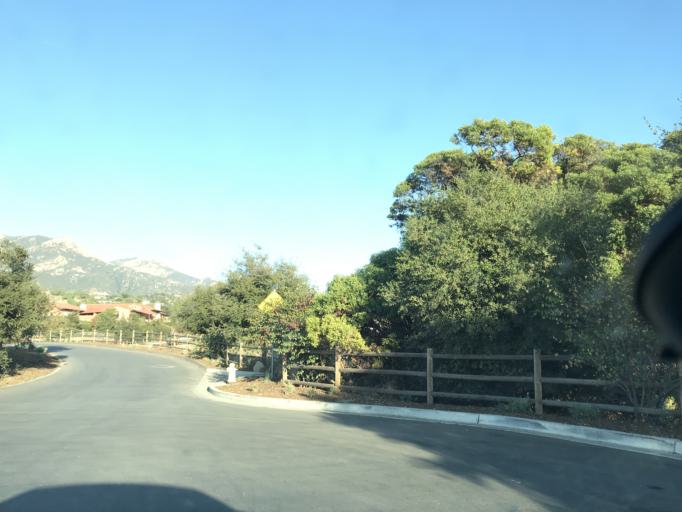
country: US
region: California
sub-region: Santa Barbara County
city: Mission Canyon
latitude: 34.4567
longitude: -119.7589
